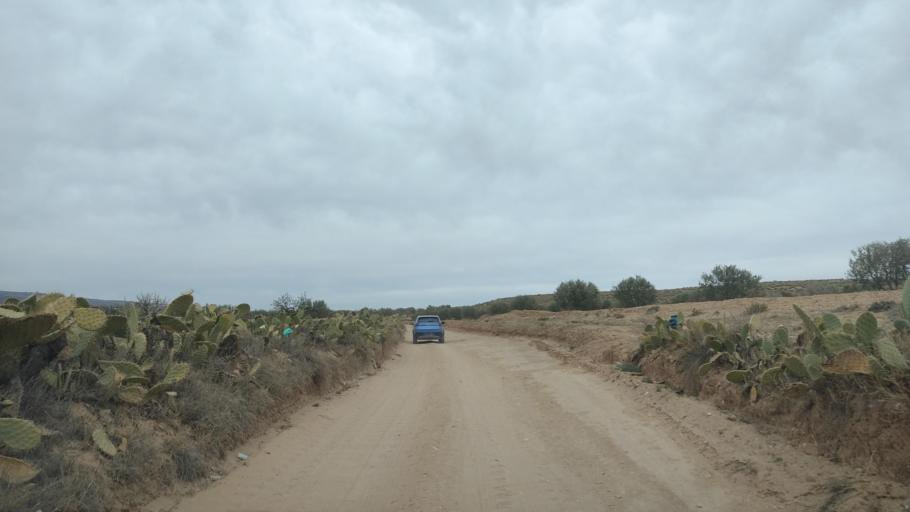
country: TN
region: Al Qasrayn
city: Kasserine
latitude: 35.2505
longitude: 8.9212
